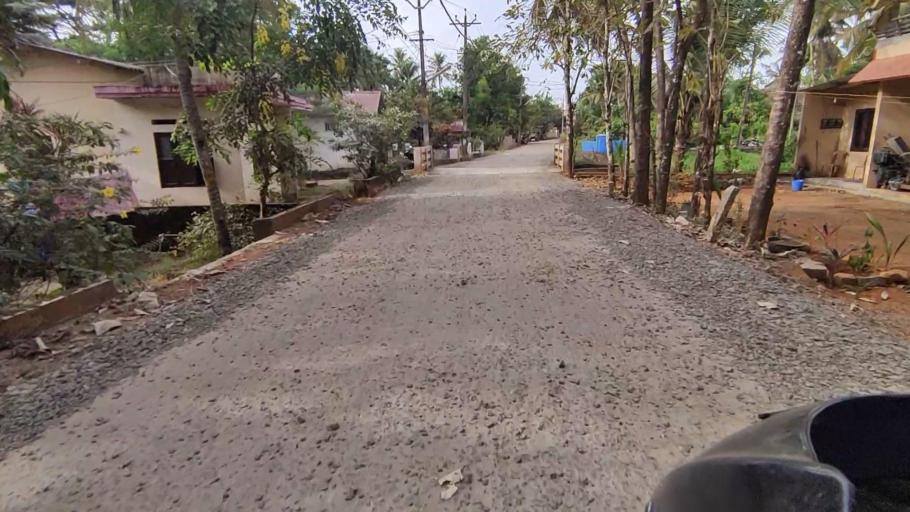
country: IN
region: Kerala
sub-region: Kottayam
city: Kottayam
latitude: 9.5831
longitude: 76.4914
